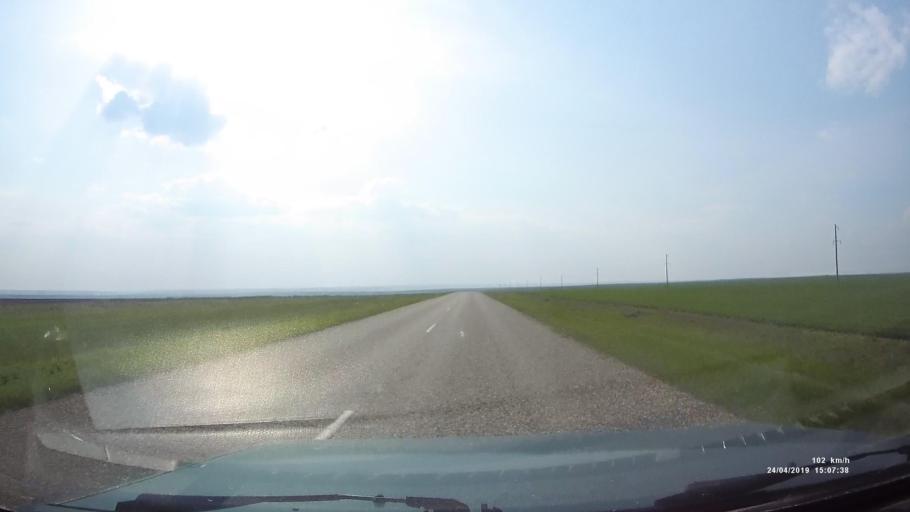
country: RU
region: Rostov
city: Remontnoye
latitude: 46.5598
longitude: 43.4009
